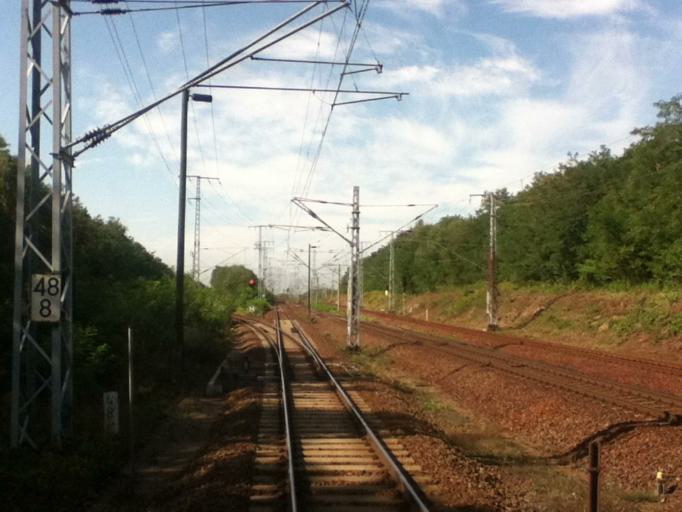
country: DE
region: Brandenburg
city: Senftenberg
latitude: 51.5469
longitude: 14.0429
